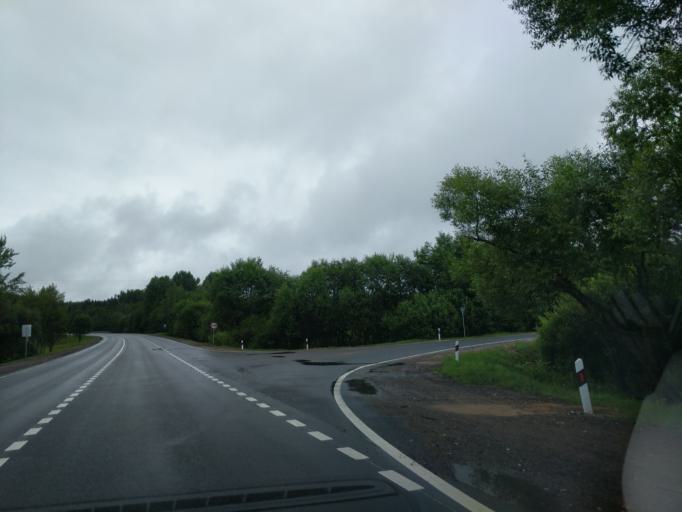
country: BY
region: Minsk
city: Syomkava
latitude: 54.2090
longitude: 27.4964
